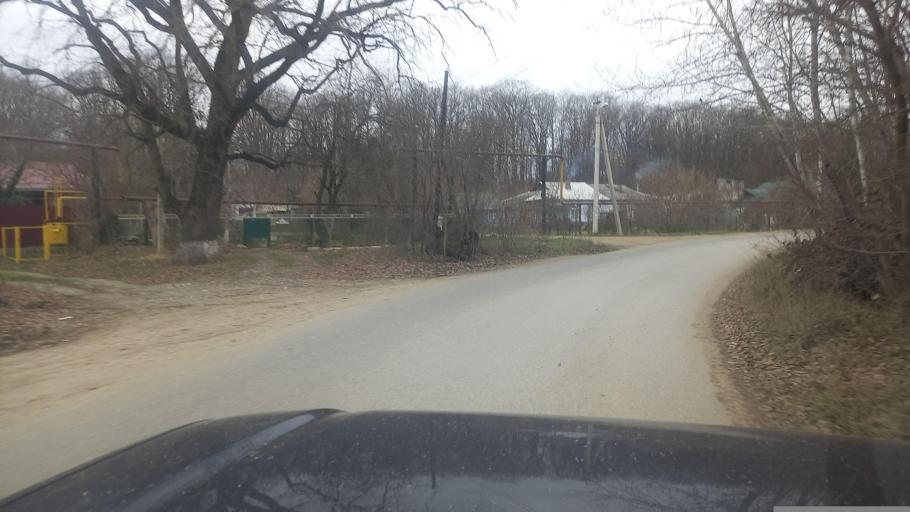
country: RU
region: Adygeya
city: Maykop
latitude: 44.5730
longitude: 40.0704
